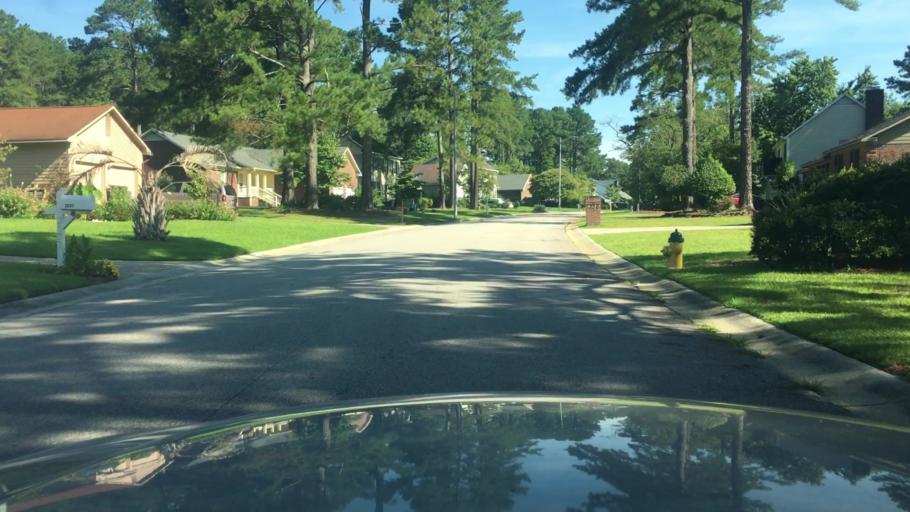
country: US
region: North Carolina
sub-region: Cumberland County
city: Fayetteville
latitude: 35.1122
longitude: -78.9028
